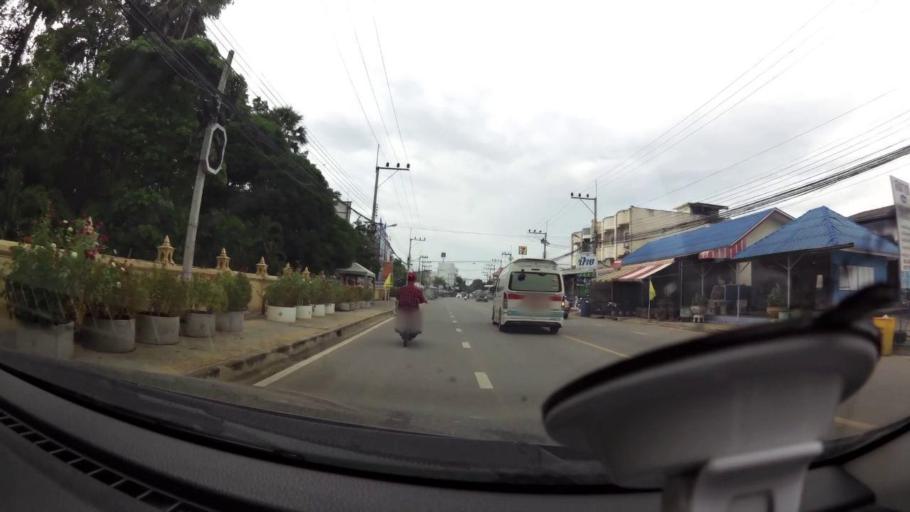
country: TH
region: Prachuap Khiri Khan
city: Pran Buri
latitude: 12.3966
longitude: 99.9898
